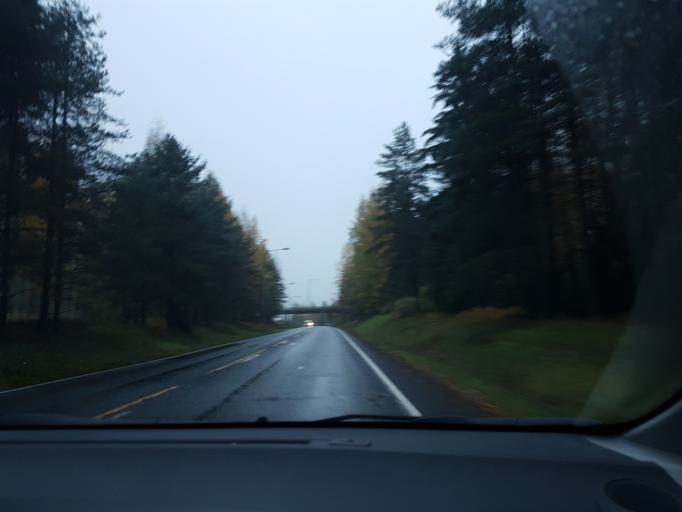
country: FI
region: Uusimaa
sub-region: Helsinki
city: Jaervenpaeae
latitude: 60.5049
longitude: 25.0961
